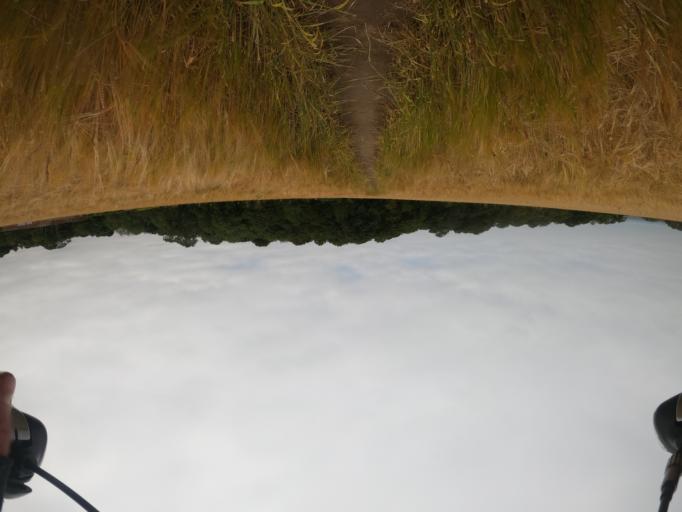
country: GB
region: Scotland
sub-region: East Lothian
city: Musselburgh
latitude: 55.9423
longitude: -3.0836
